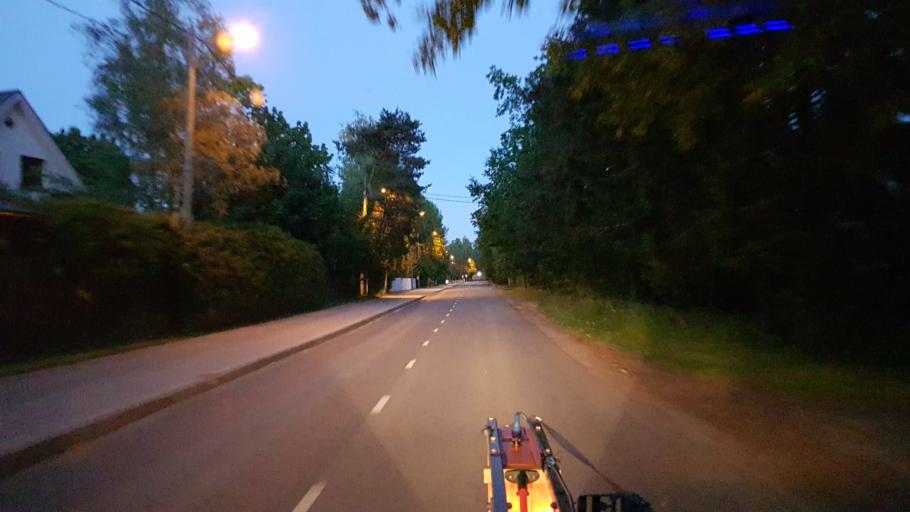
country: EE
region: Harju
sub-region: Harku vald
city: Tabasalu
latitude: 59.4447
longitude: 24.5922
